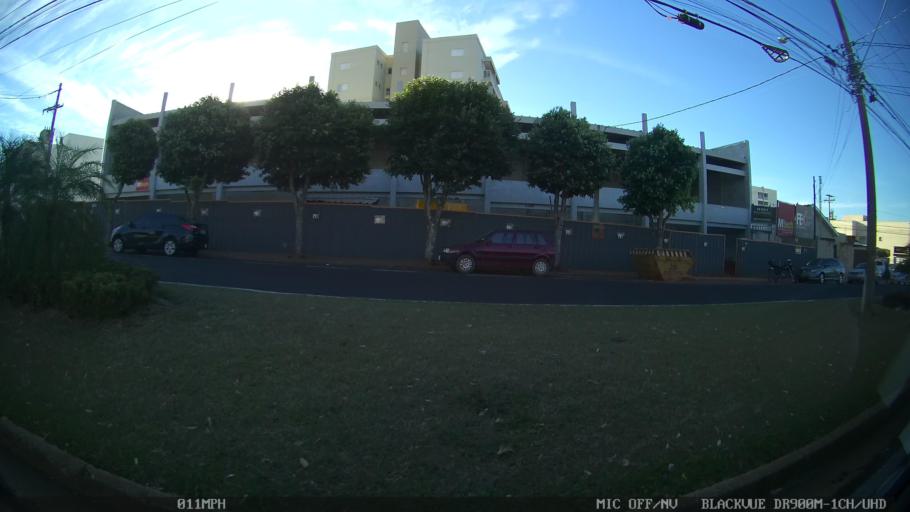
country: BR
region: Sao Paulo
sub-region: Sao Jose Do Rio Preto
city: Sao Jose do Rio Preto
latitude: -20.8278
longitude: -49.3719
